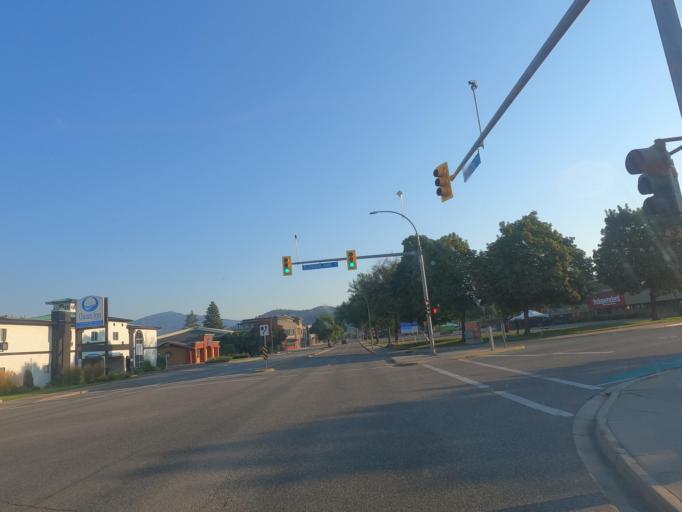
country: CA
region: British Columbia
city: Kelowna
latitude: 49.8799
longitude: -119.4769
